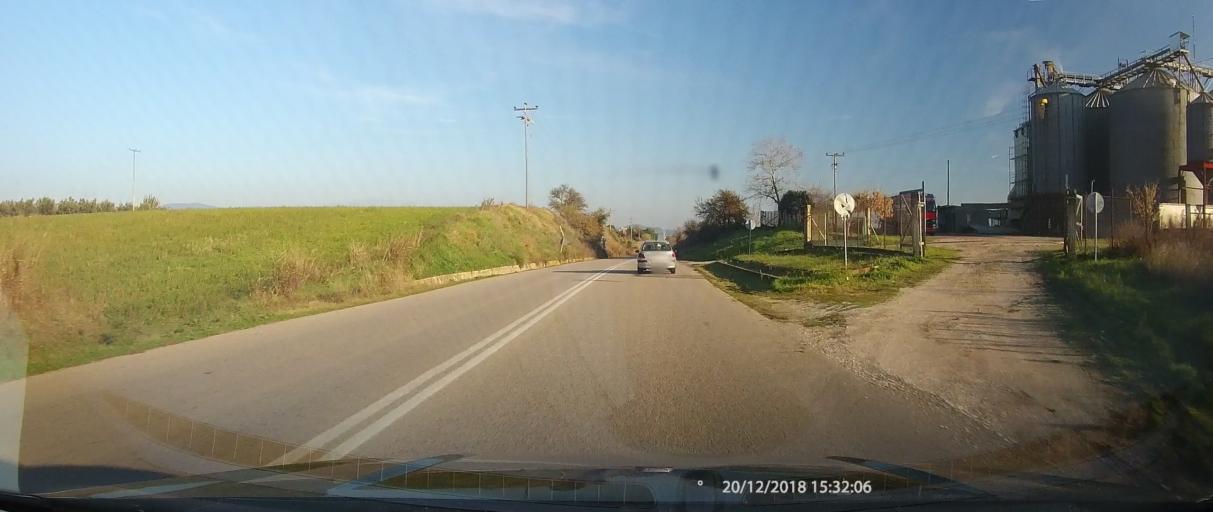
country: GR
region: Central Greece
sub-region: Nomos Fthiotidos
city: Lianokladhion
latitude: 38.9297
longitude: 22.2526
